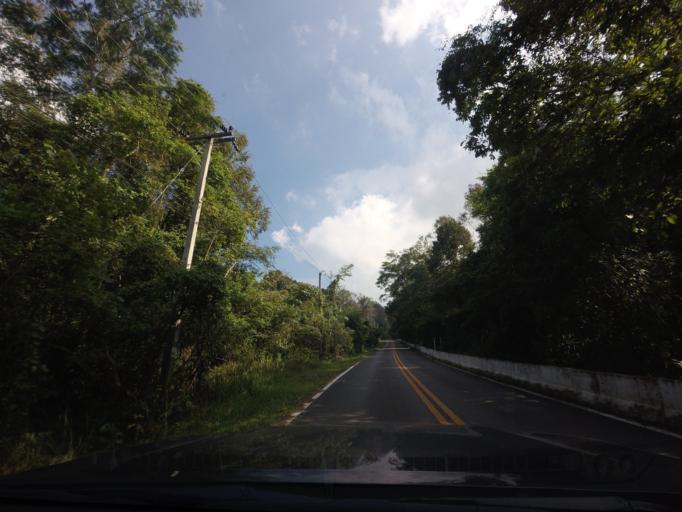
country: TH
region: Phitsanulok
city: Nakhon Thai
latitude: 16.9913
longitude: 101.0125
